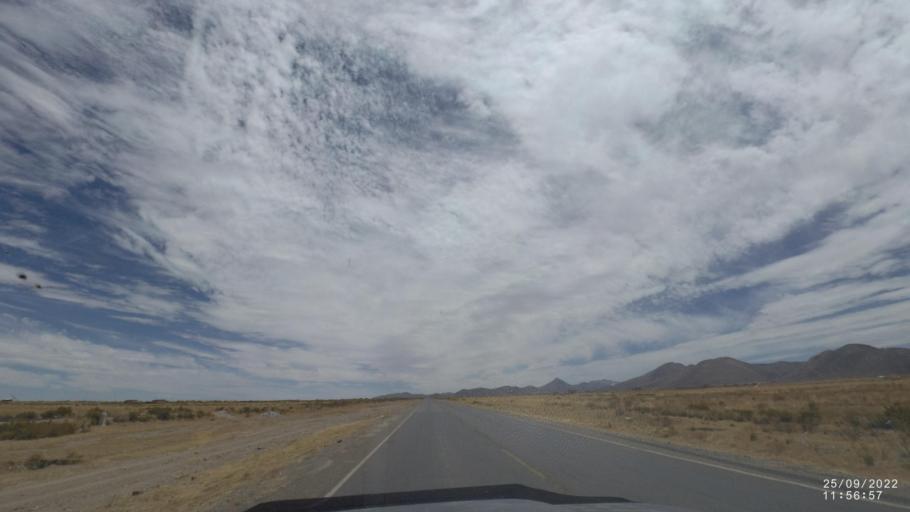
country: BO
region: Oruro
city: Challapata
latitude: -18.8314
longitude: -66.8233
